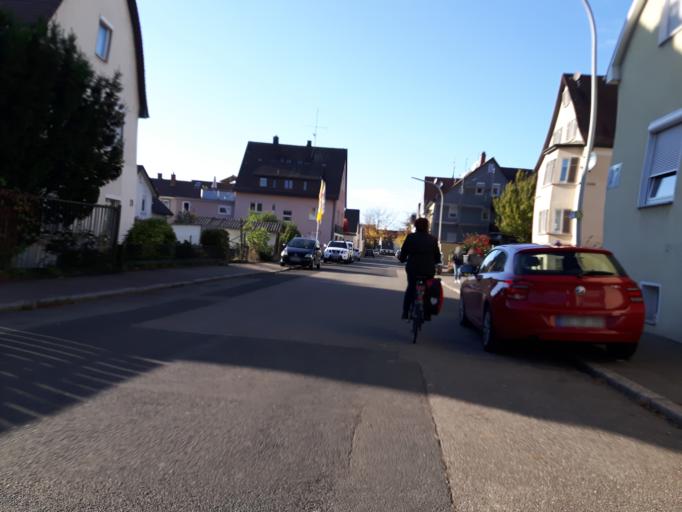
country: DE
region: Baden-Wuerttemberg
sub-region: Regierungsbezirk Stuttgart
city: Flein
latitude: 49.1177
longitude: 9.1929
